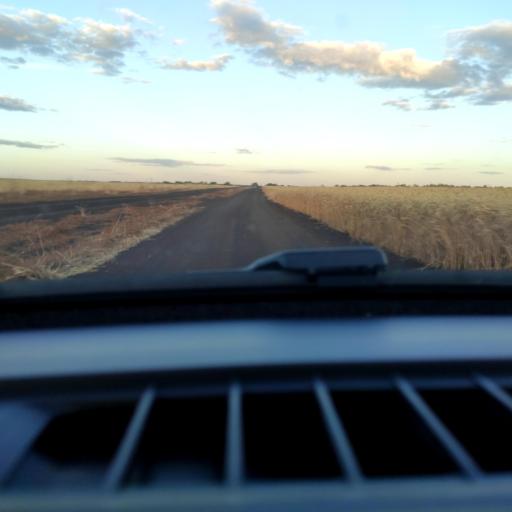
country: RU
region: Voronezj
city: Verkhnyaya Khava
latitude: 51.6108
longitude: 39.8236
